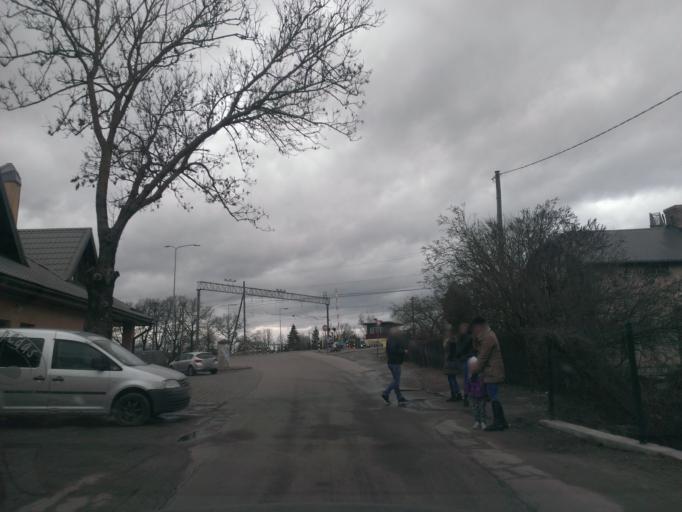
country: LV
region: Salaspils
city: Salaspils
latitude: 56.8601
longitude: 24.3501
